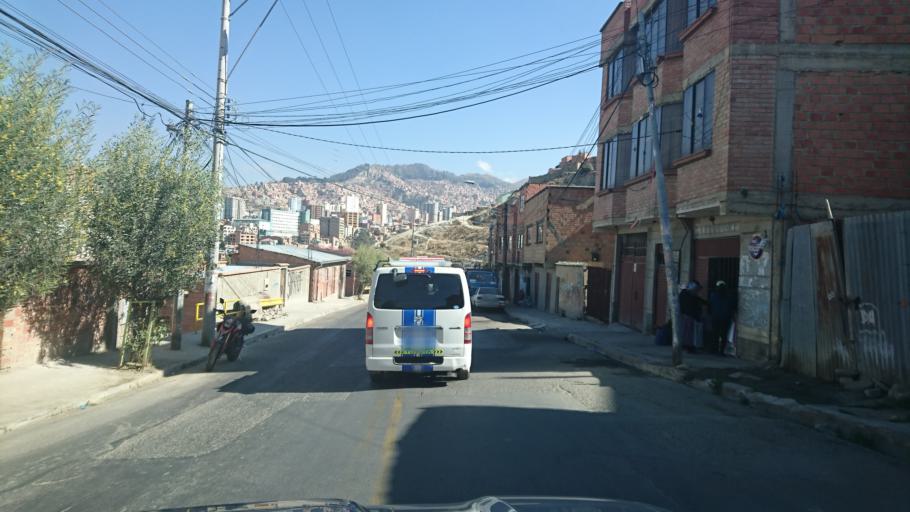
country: BO
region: La Paz
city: La Paz
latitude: -16.5030
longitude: -68.1133
